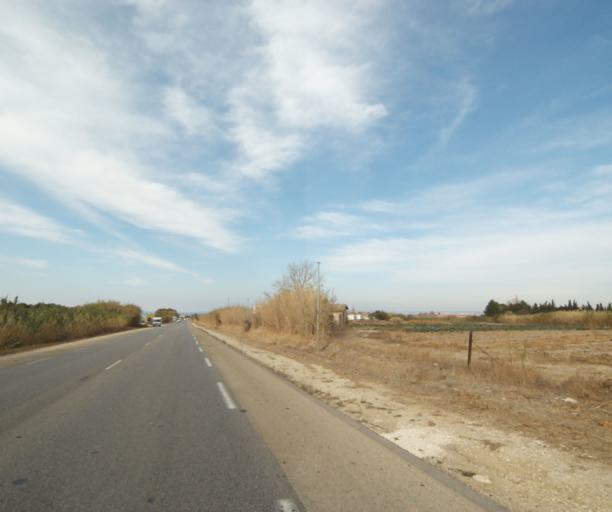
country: FR
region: Provence-Alpes-Cote d'Azur
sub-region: Departement des Bouches-du-Rhone
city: Gignac-la-Nerthe
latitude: 43.3880
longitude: 5.2137
